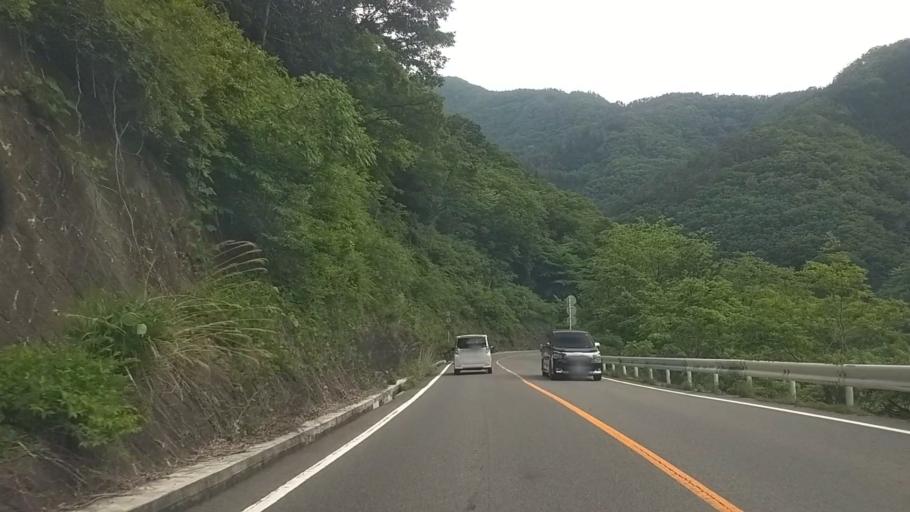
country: JP
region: Yamanashi
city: Fujikawaguchiko
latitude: 35.5391
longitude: 138.5940
